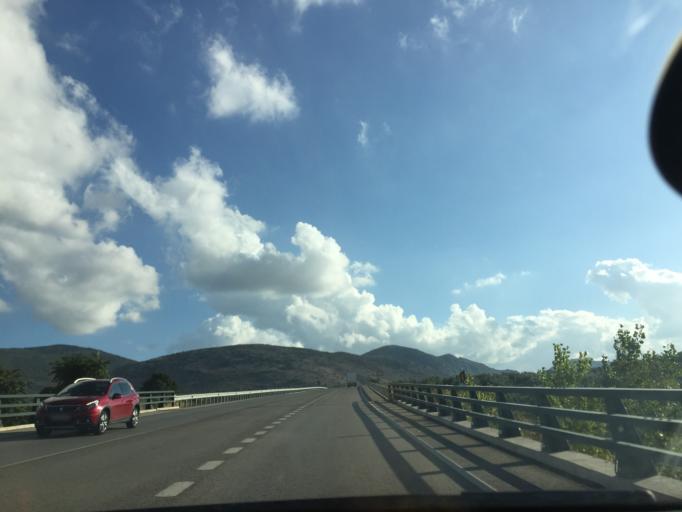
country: ES
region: Andalusia
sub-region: Provincia de Jaen
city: Mancha Real
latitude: 37.7930
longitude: -3.6220
